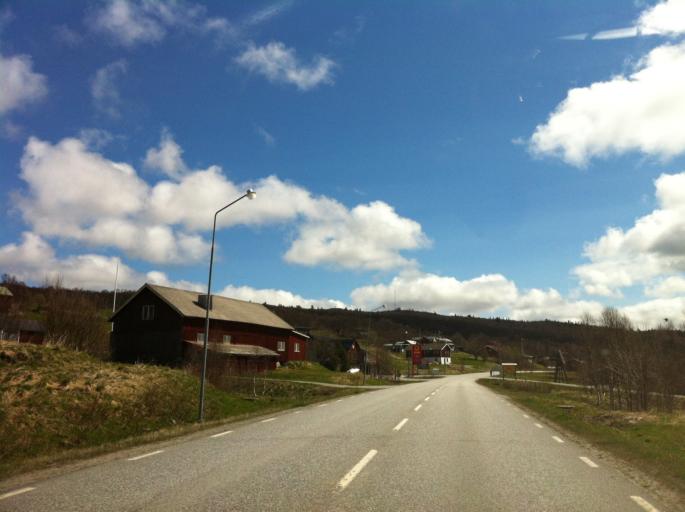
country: NO
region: Sor-Trondelag
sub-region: Tydal
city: Aas
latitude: 62.6404
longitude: 12.4378
